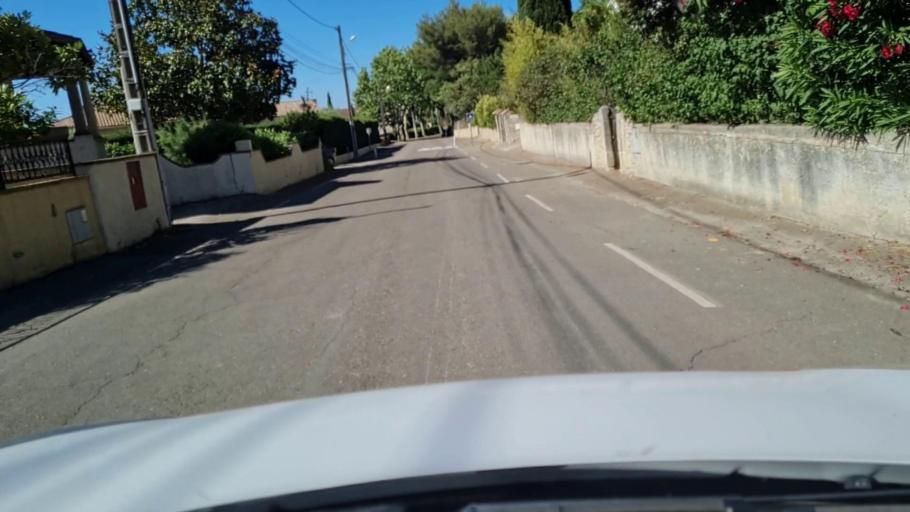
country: FR
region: Languedoc-Roussillon
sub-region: Departement du Gard
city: Calvisson
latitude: 43.7798
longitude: 4.1895
